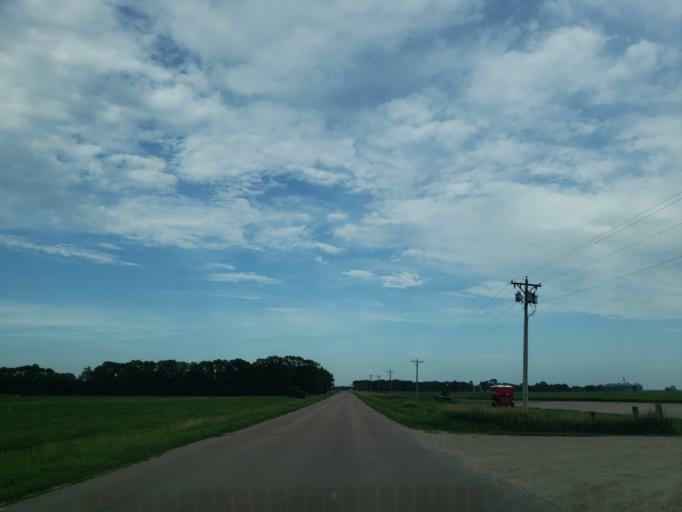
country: US
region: South Dakota
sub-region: Davison County
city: Mitchell
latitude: 43.6878
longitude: -97.9964
